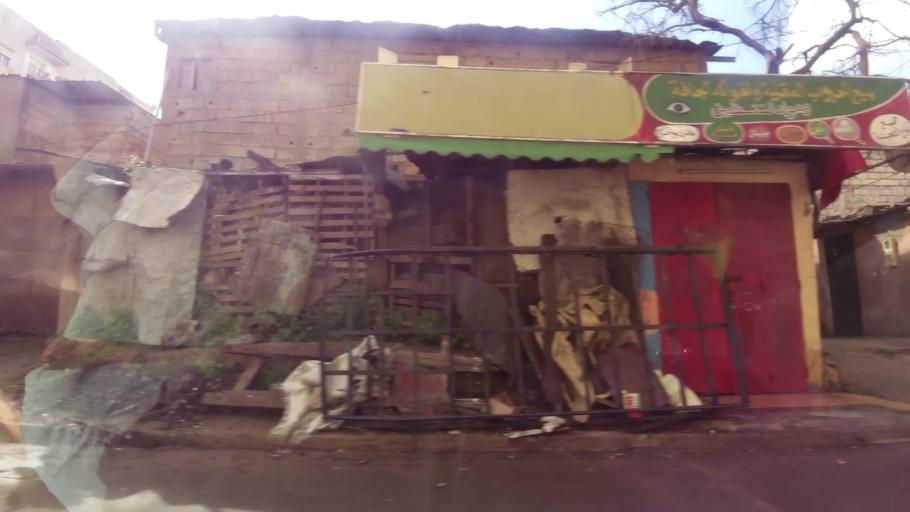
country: MA
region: Grand Casablanca
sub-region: Nouaceur
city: Bouskoura
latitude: 33.5300
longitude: -7.6855
